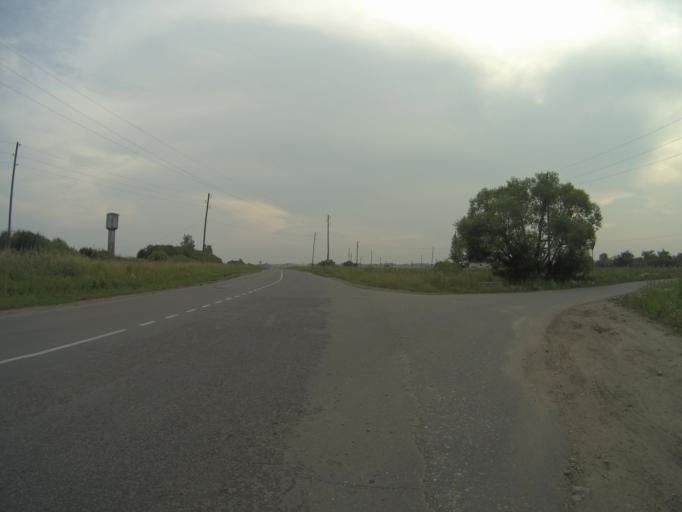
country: RU
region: Vladimir
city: Suzdal'
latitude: 56.3875
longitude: 40.2800
